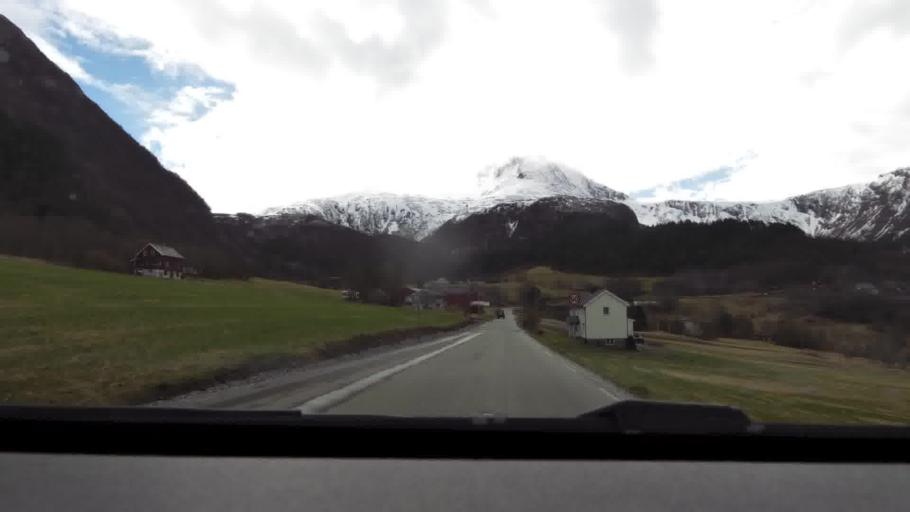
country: NO
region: More og Romsdal
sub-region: Kristiansund
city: Kristiansund
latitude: 63.1169
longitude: 7.7498
